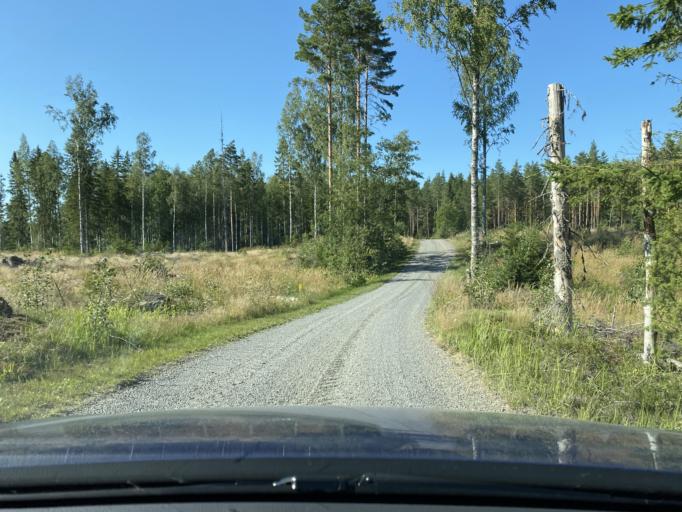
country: FI
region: Satakunta
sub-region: Rauma
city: Kiukainen
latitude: 61.1443
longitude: 22.0222
